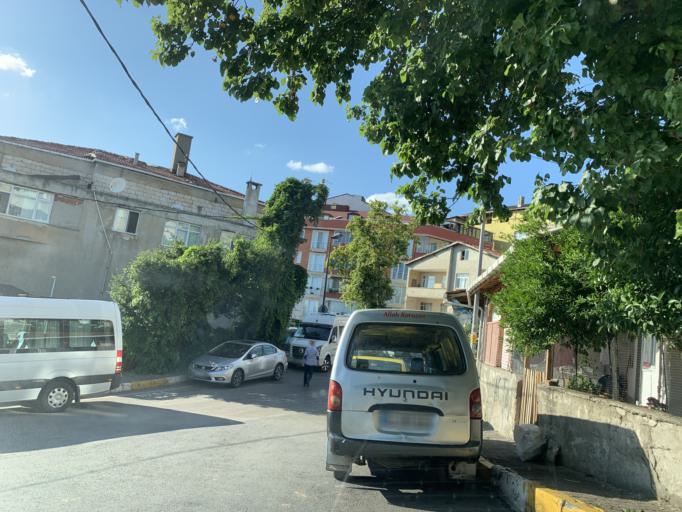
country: TR
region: Istanbul
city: Pendik
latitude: 40.8892
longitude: 29.2446
